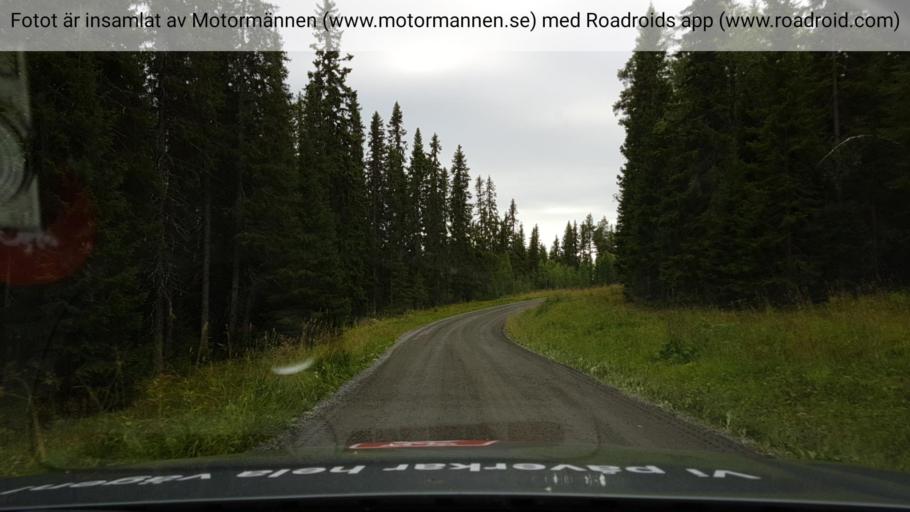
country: SE
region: Jaemtland
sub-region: Krokoms Kommun
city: Valla
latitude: 63.3914
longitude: 14.0614
